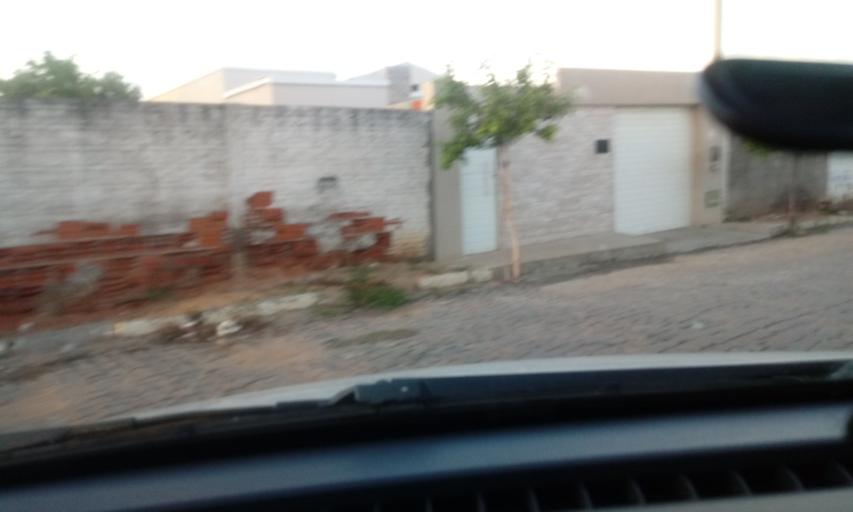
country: BR
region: Bahia
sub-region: Riacho De Santana
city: Riacho de Santana
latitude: -13.9098
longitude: -42.8479
